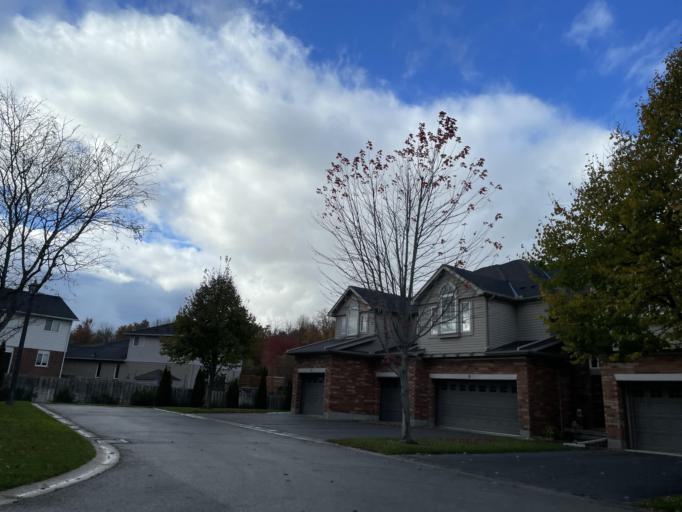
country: CA
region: Ontario
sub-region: Wellington County
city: Guelph
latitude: 43.5266
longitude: -80.3022
